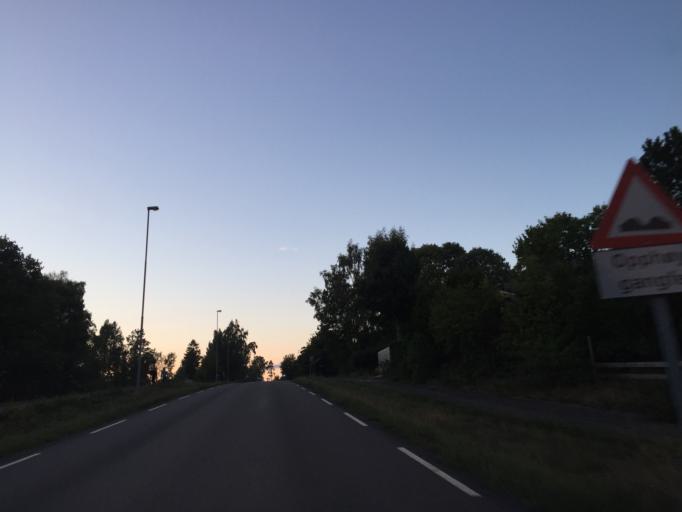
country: NO
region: Ostfold
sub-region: Moss
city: Moss
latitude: 59.4990
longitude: 10.6867
